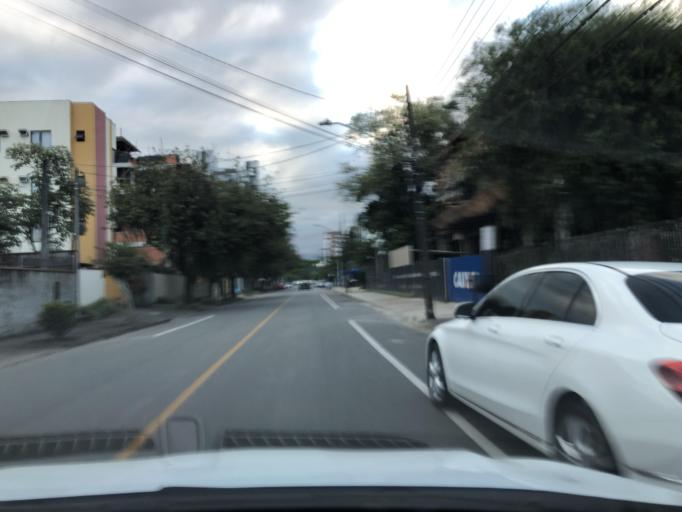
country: BR
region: Santa Catarina
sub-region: Joinville
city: Joinville
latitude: -26.2755
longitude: -48.8513
